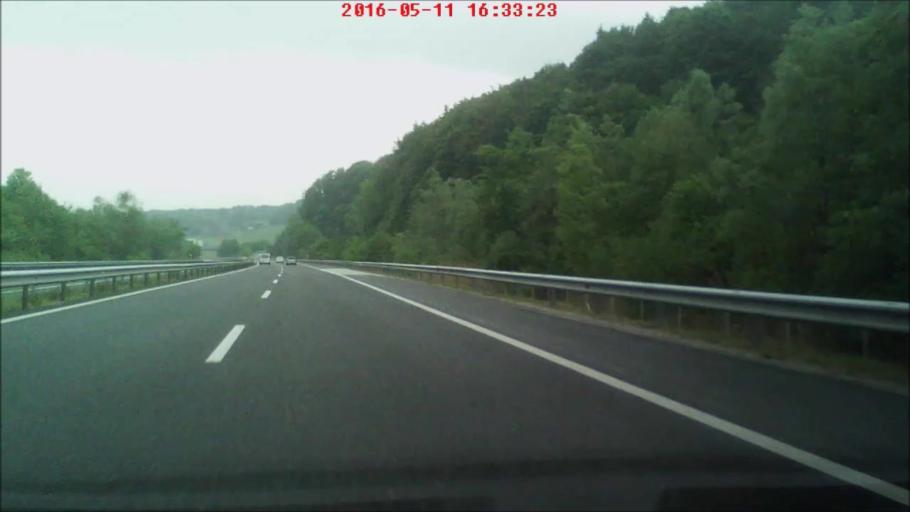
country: SI
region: Pesnica
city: Pesnica pri Mariboru
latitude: 46.6291
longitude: 15.6579
